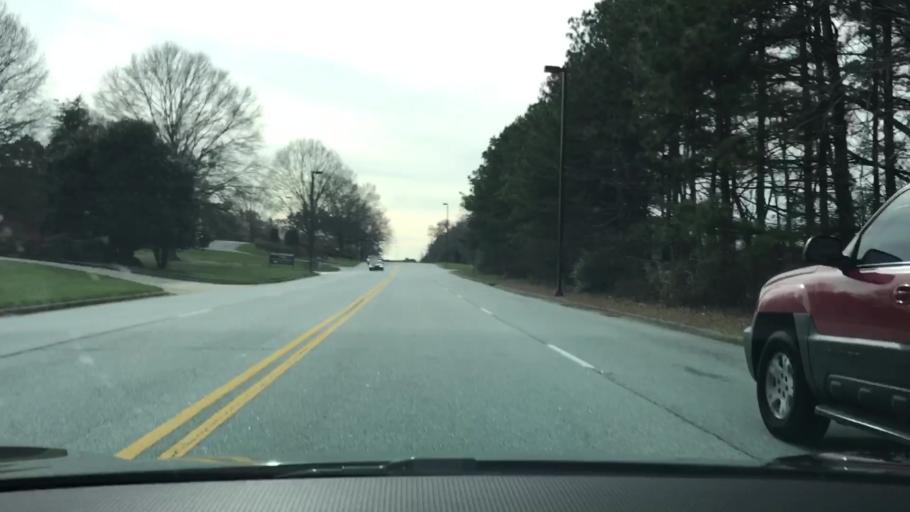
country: US
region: Georgia
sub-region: Gwinnett County
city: Suwanee
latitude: 34.0149
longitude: -84.0619
